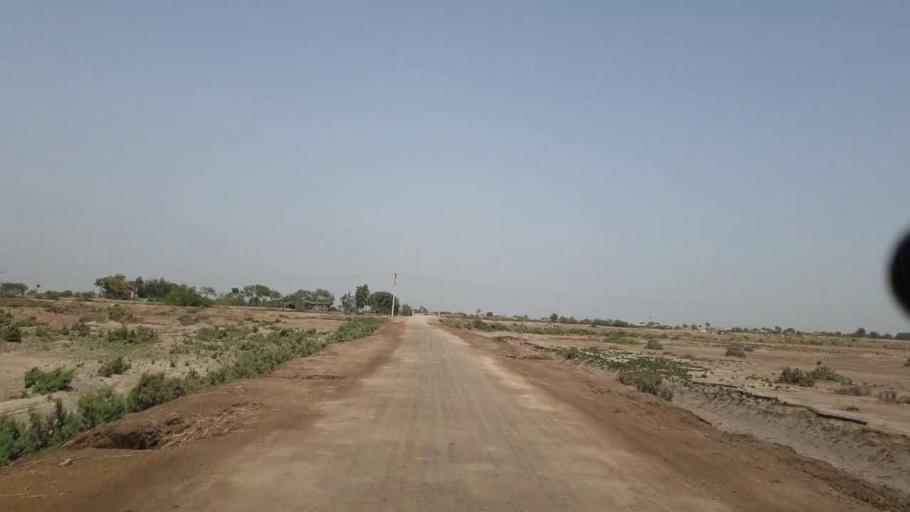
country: PK
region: Sindh
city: Matli
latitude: 25.0748
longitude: 68.6893
